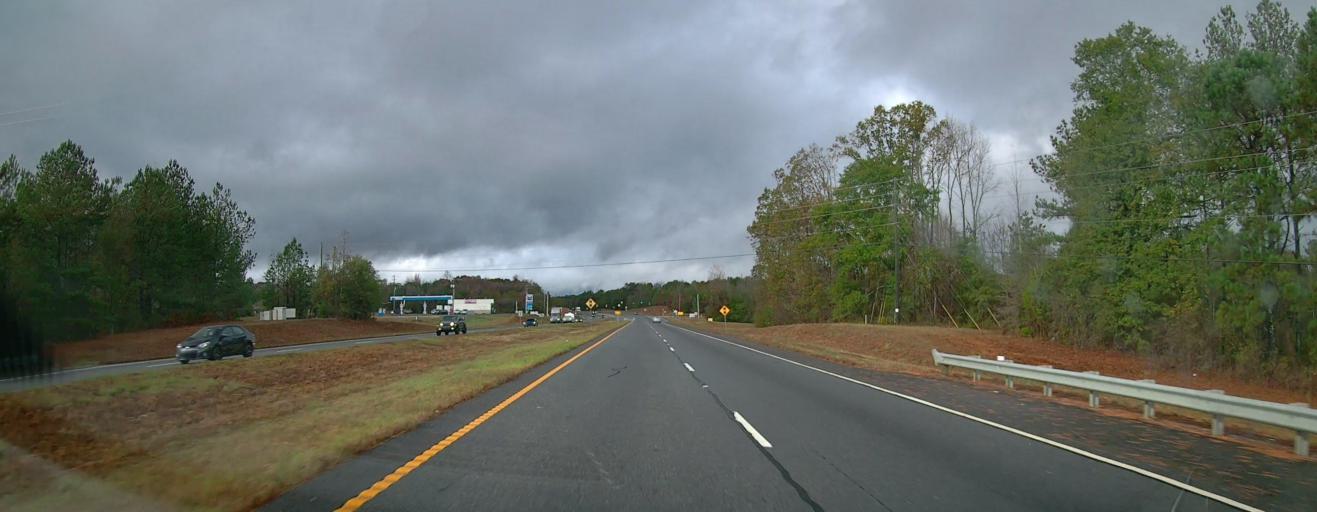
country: US
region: Georgia
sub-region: Clarke County
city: Country Club Estates
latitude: 34.0463
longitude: -83.4050
